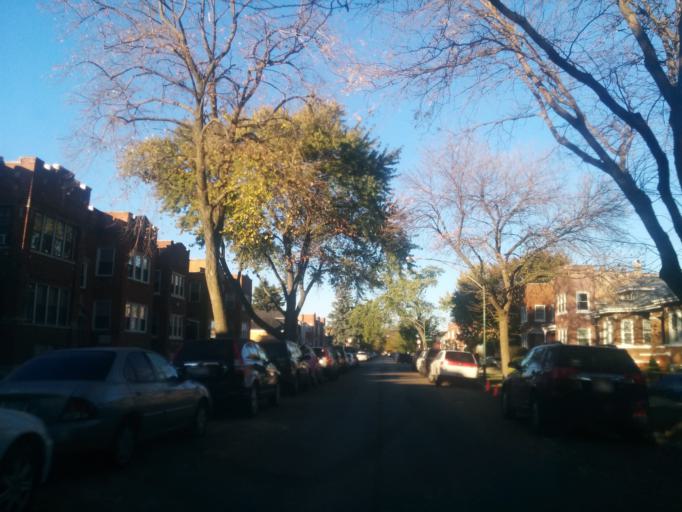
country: US
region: Illinois
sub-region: Cook County
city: Oak Park
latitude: 41.9270
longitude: -87.7529
